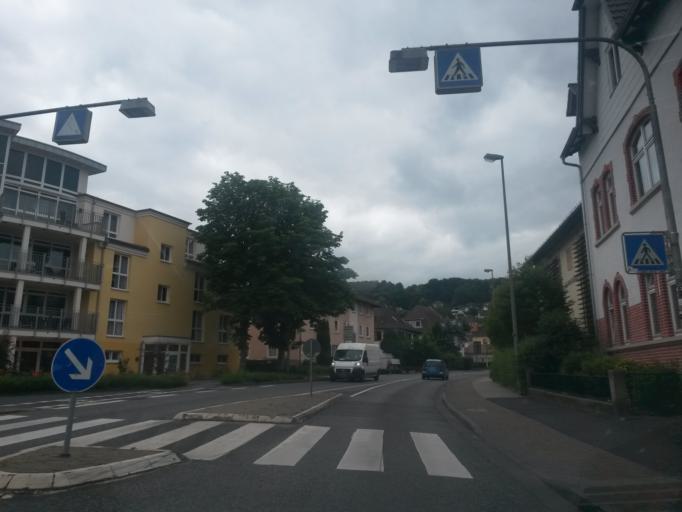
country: DE
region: Hesse
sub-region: Regierungsbezirk Kassel
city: Bad Hersfeld
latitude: 50.8650
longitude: 9.7023
